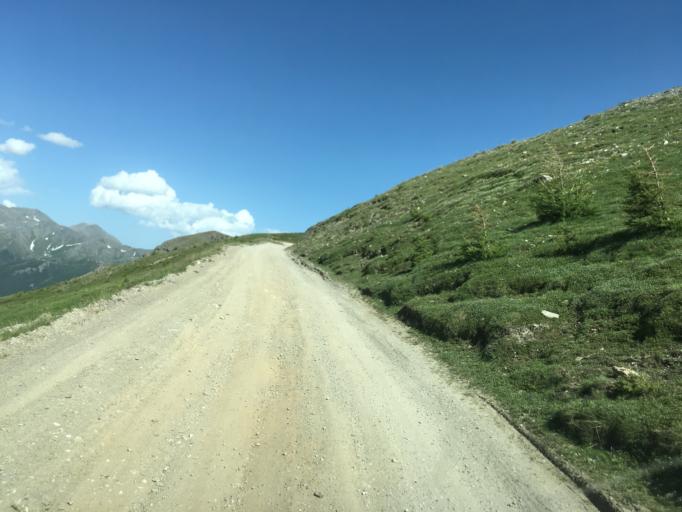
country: IT
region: Piedmont
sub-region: Provincia di Torino
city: Sestriere
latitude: 44.9861
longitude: 6.8706
